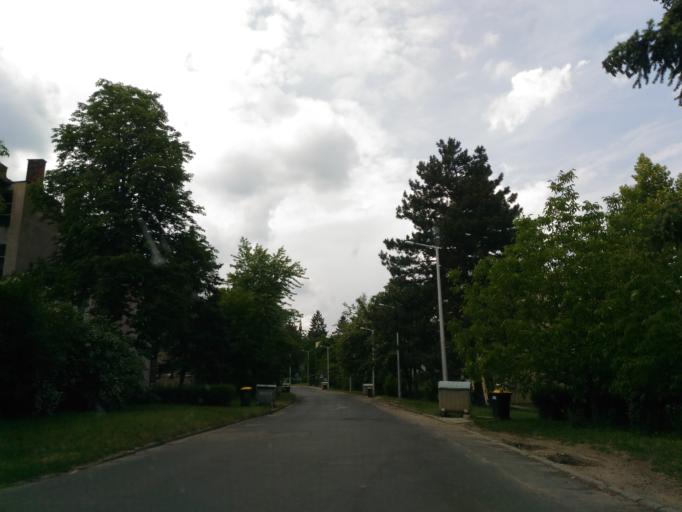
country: HU
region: Baranya
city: Komlo
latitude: 46.1866
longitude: 18.2568
